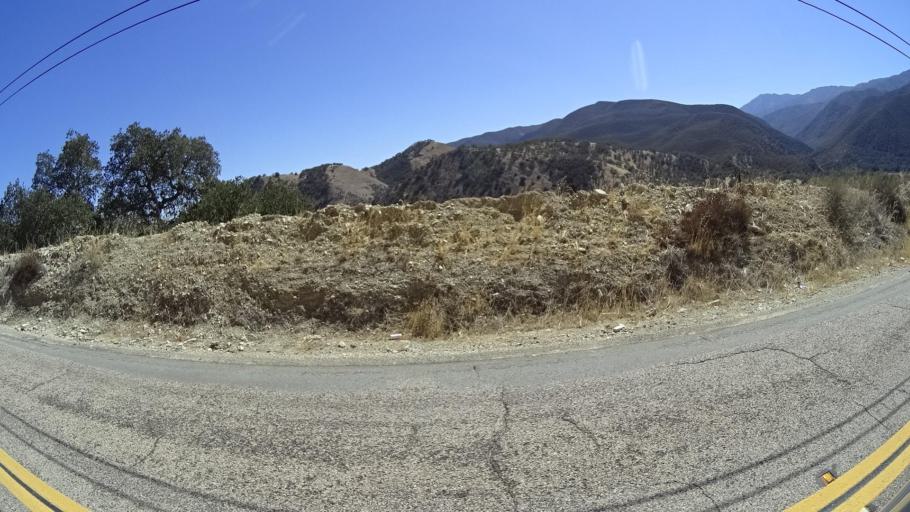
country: US
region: California
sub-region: Monterey County
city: Greenfield
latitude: 36.2624
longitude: -121.4181
